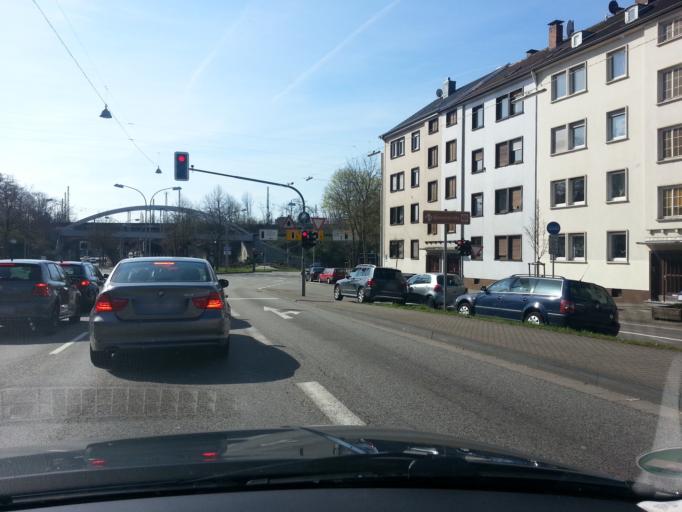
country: DE
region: Saarland
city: Saarbrucken
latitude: 49.2443
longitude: 6.9812
